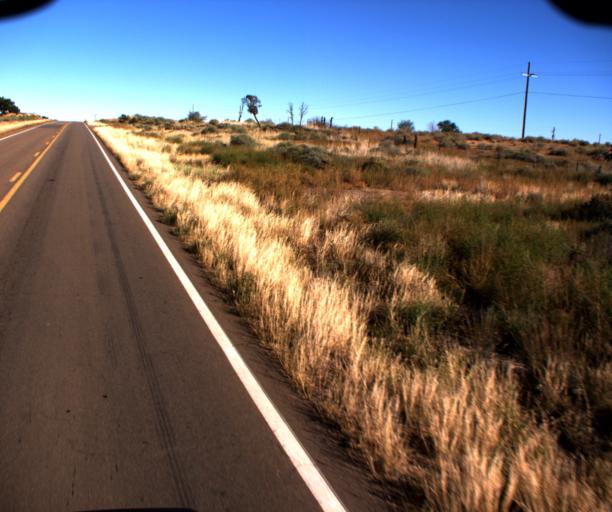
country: US
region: Arizona
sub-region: Navajo County
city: Snowflake
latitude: 34.5600
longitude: -110.0814
